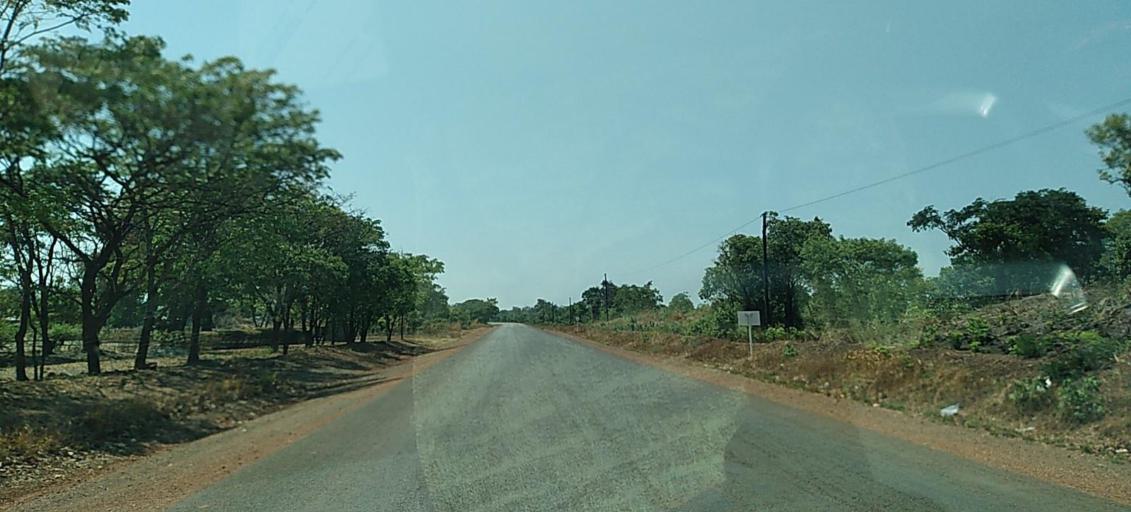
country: ZM
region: North-Western
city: Solwezi
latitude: -12.3583
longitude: 25.9312
